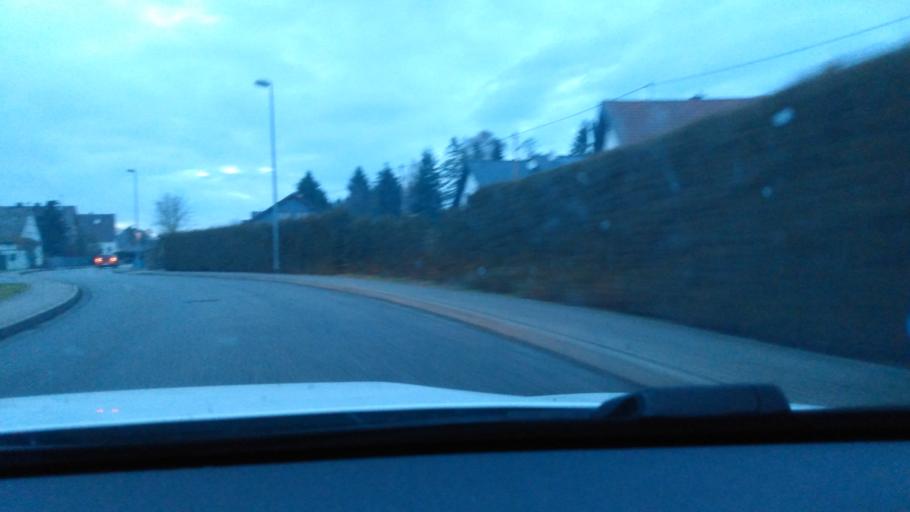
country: DE
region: Rheinland-Pfalz
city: Kircheib
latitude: 50.6972
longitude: 7.4363
